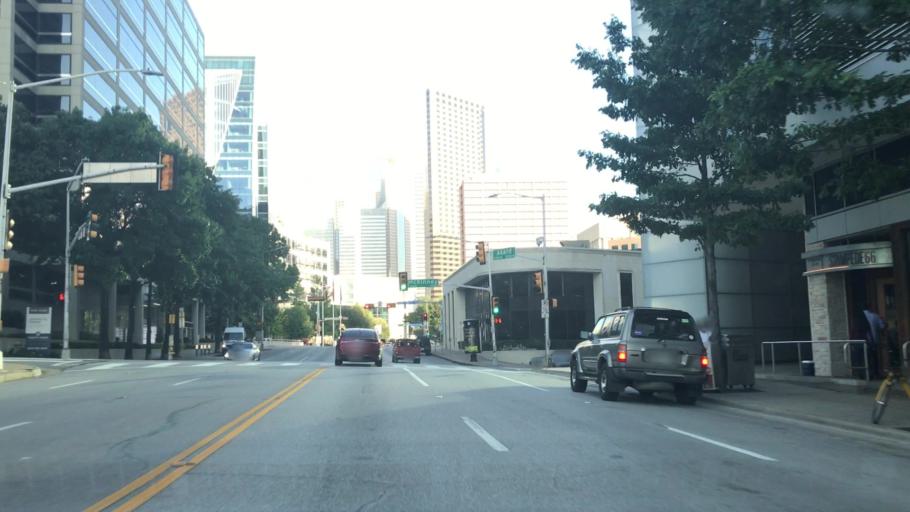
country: US
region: Texas
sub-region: Dallas County
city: Dallas
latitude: 32.7890
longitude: -96.8046
